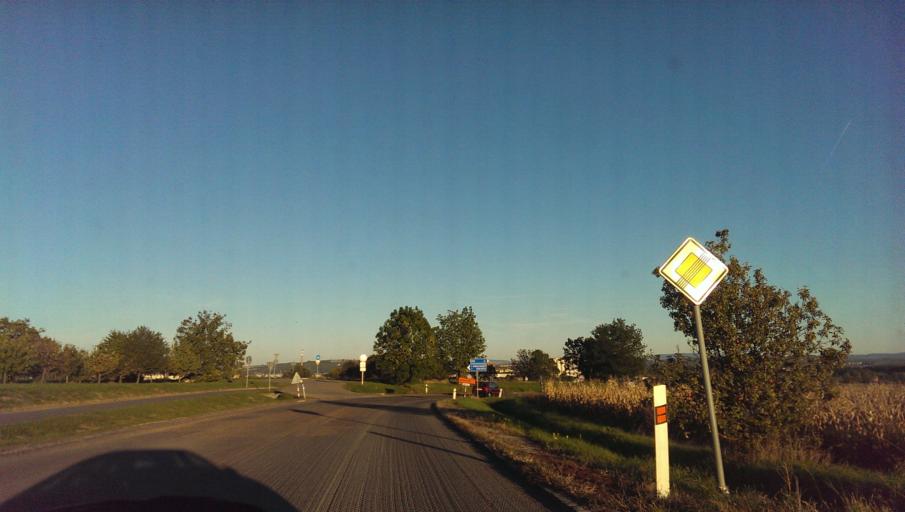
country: CZ
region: Zlin
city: Zlechov
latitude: 49.0741
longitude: 17.3992
